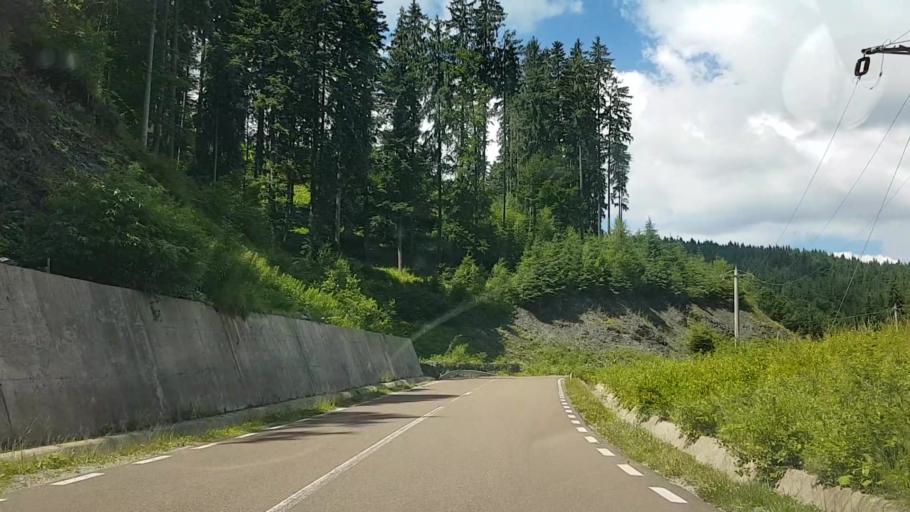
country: RO
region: Suceava
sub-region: Comuna Sadova
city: Sadova
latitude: 47.4630
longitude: 25.5167
